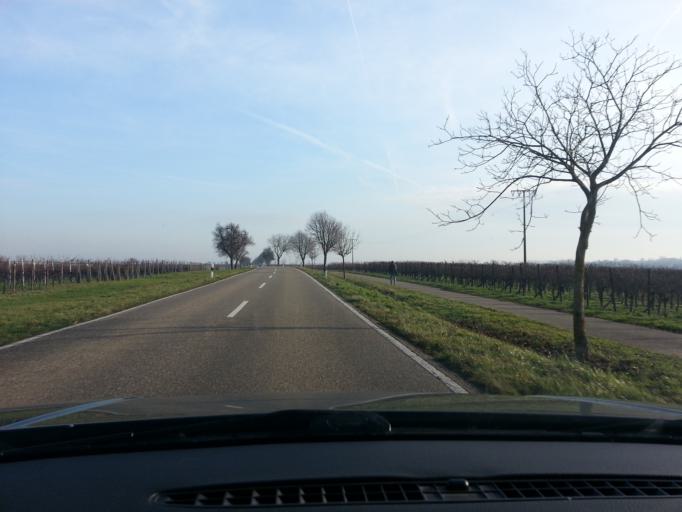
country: DE
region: Rheinland-Pfalz
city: Heuchelheim-Klingen
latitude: 49.1432
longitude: 8.0664
